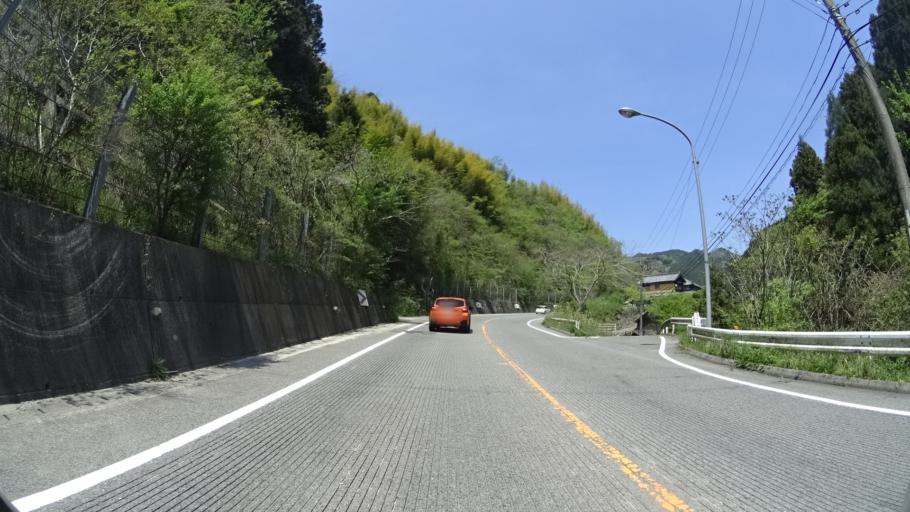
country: JP
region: Ehime
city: Hojo
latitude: 33.9247
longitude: 132.8896
